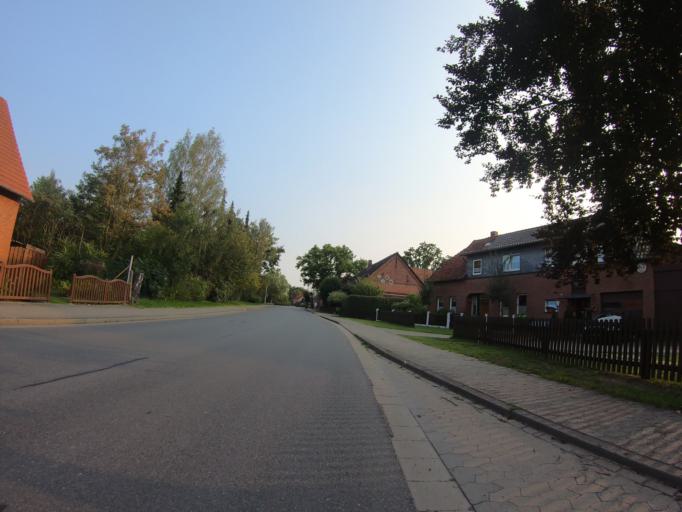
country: DE
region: Lower Saxony
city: Leiferde
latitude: 52.4404
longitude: 10.4354
